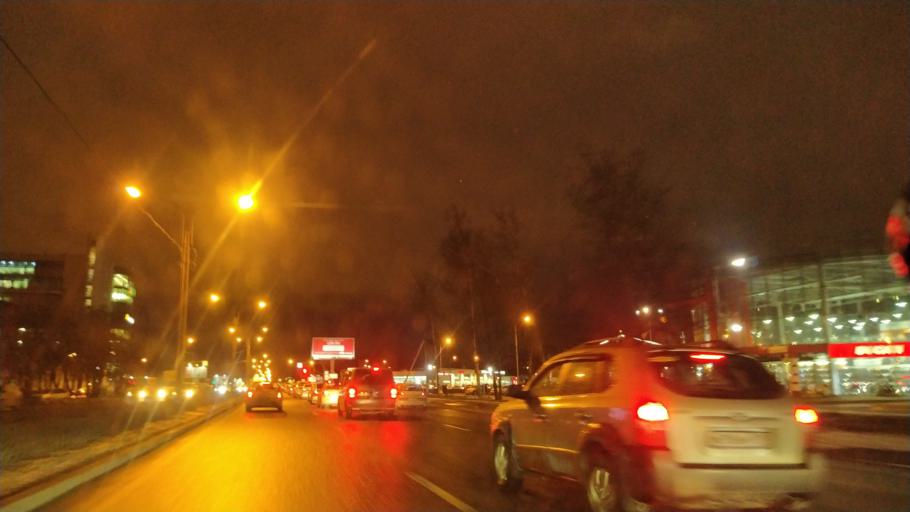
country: RU
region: St.-Petersburg
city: Kupchino
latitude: 59.8324
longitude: 30.3413
